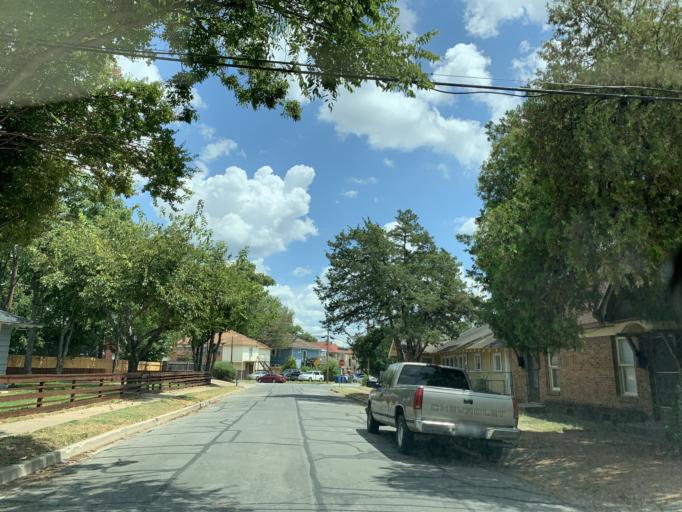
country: US
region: Texas
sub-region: Dallas County
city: Cockrell Hill
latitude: 32.7509
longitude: -96.8422
